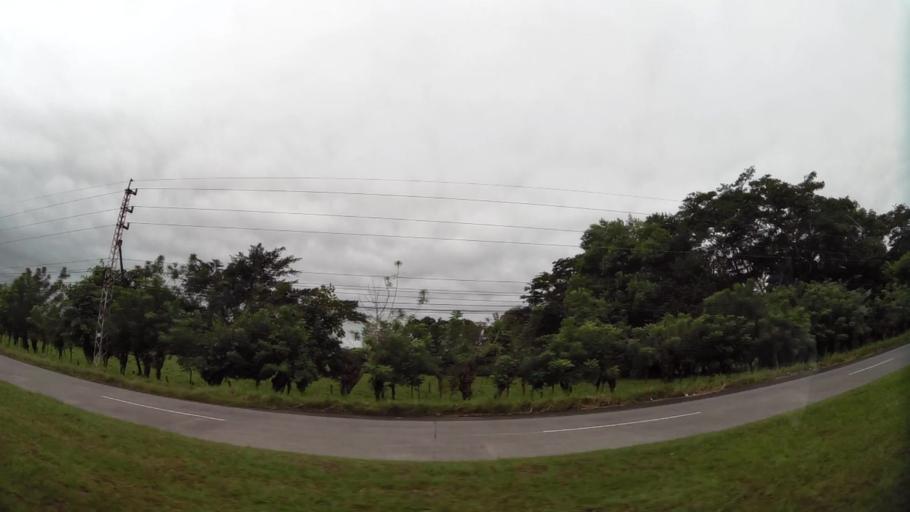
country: PA
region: Chiriqui
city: Tijera
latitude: 8.4779
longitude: -82.5515
